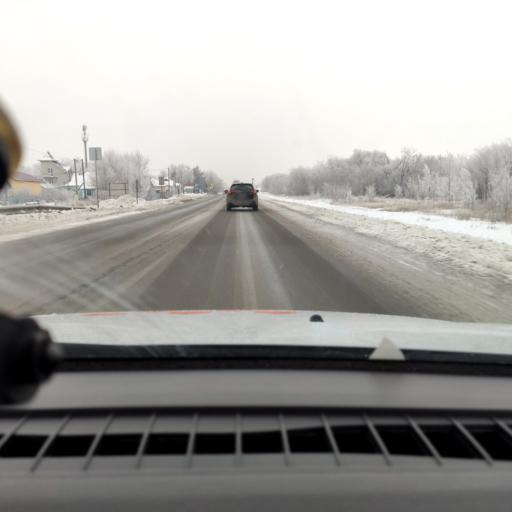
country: RU
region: Samara
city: Samara
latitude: 53.0866
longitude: 50.1571
